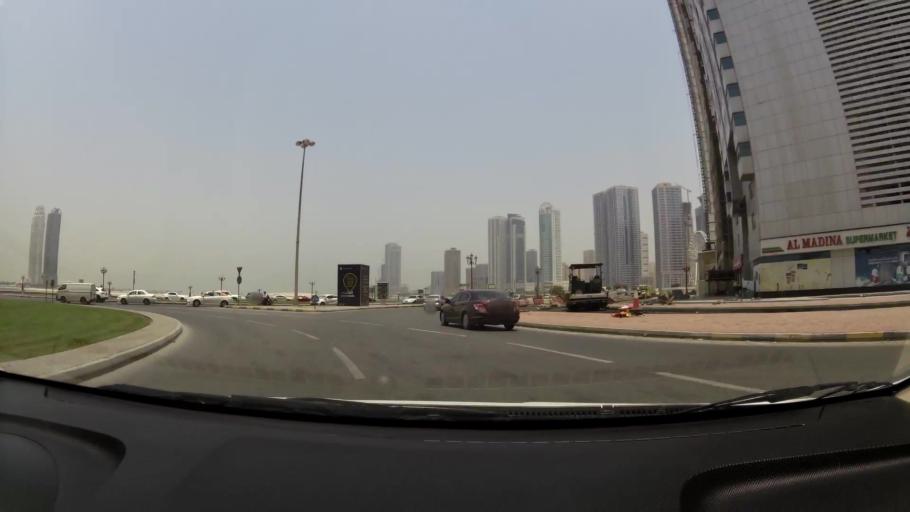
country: AE
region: Ash Shariqah
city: Sharjah
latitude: 25.3184
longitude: 55.3746
